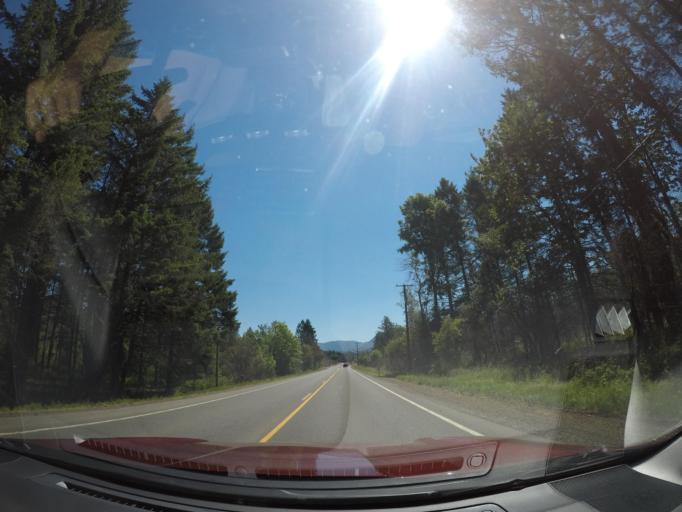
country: US
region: Oregon
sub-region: Linn County
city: Mill City
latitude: 44.7564
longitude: -122.4237
